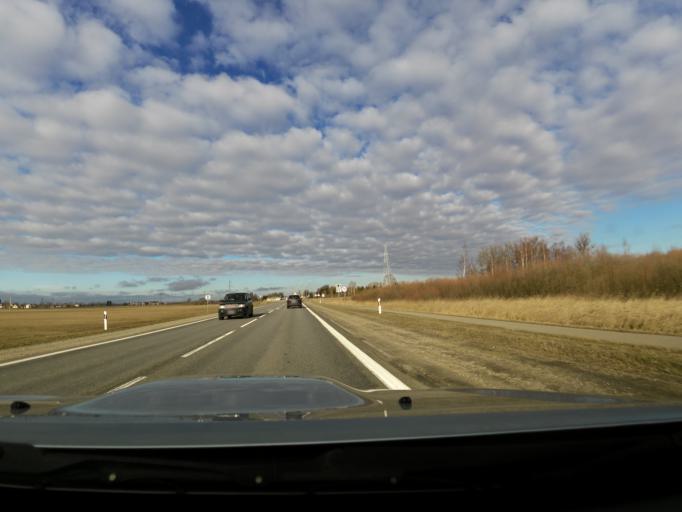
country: LT
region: Panevezys
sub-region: Panevezys City
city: Panevezys
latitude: 55.7417
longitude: 24.1834
